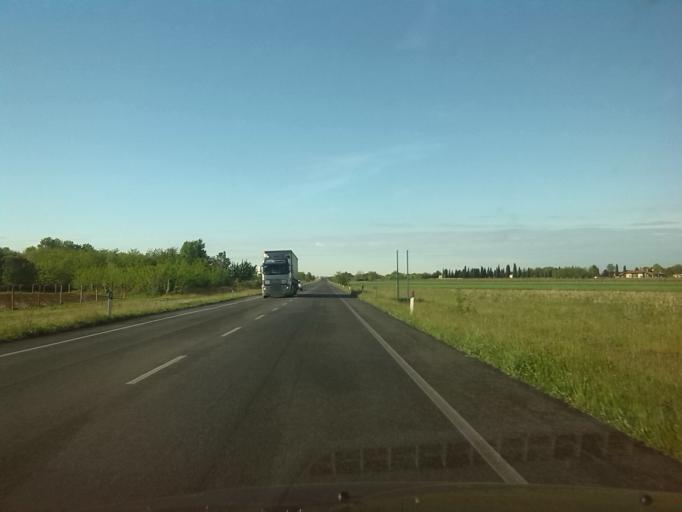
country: IT
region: Friuli Venezia Giulia
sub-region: Provincia di Gorizia
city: Mariano del Friuli
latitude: 45.9156
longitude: 13.4682
